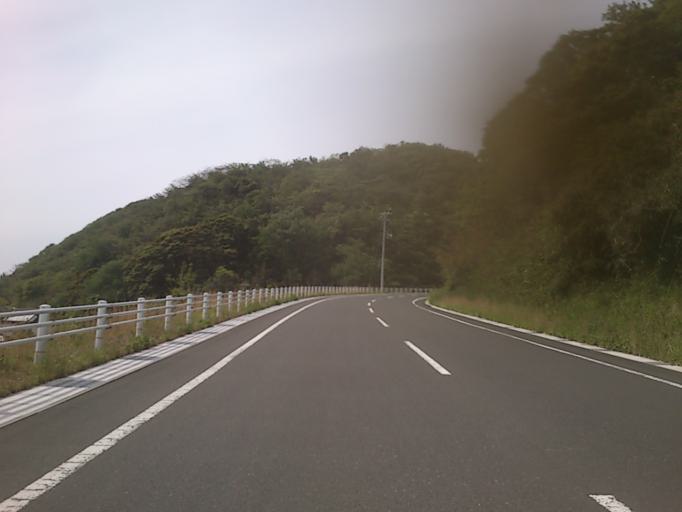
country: JP
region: Hyogo
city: Toyooka
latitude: 35.6681
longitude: 134.9708
